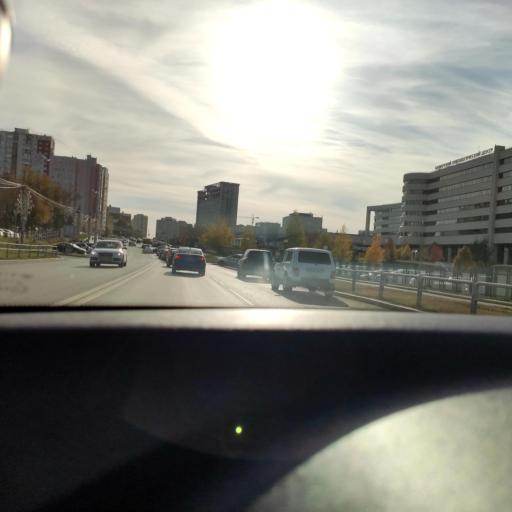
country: RU
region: Samara
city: Samara
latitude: 53.2632
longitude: 50.2101
